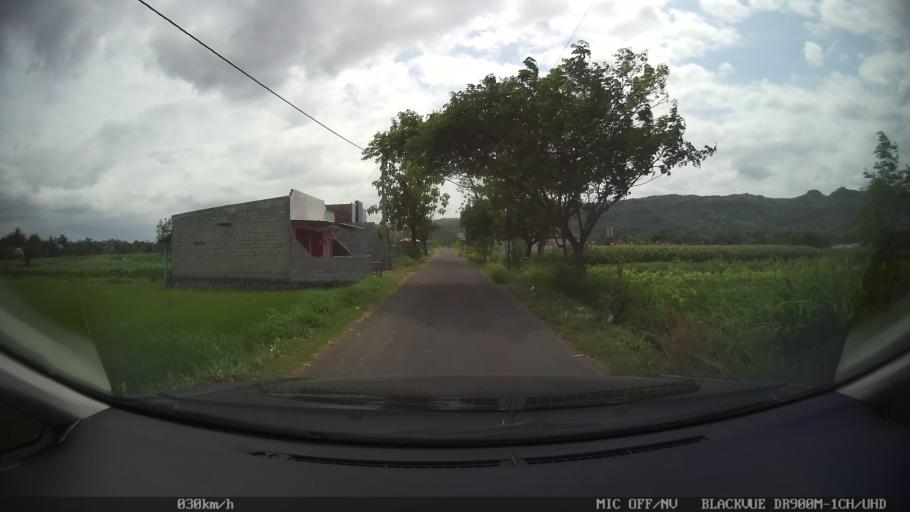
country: ID
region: Central Java
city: Candi Prambanan
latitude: -7.8110
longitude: 110.5000
